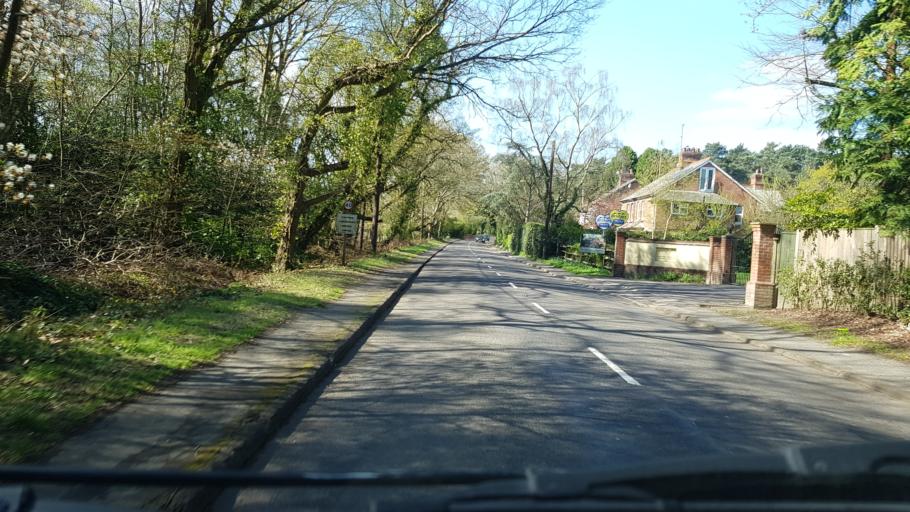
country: GB
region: England
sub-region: Surrey
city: Normandy
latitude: 51.2564
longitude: -0.6893
